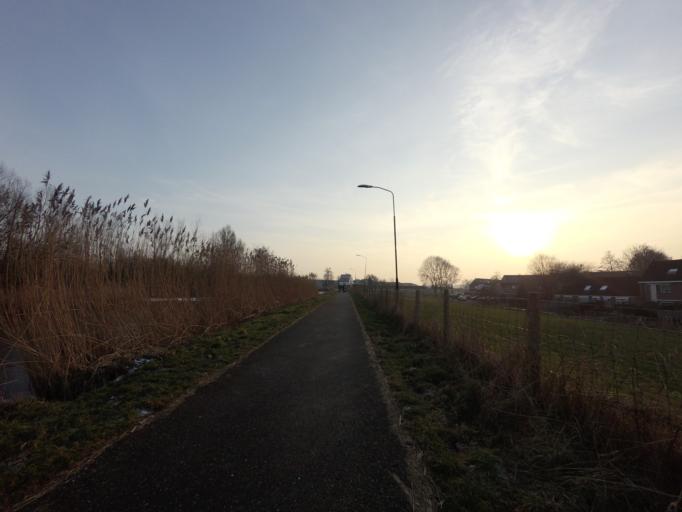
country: NL
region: Utrecht
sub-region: Gemeente De Ronde Venen
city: Mijdrecht
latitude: 52.2088
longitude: 4.9287
